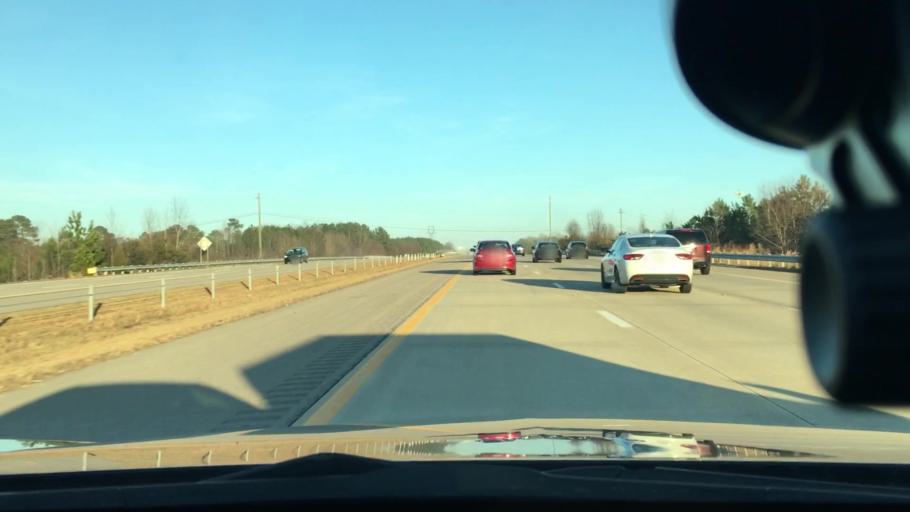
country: US
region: North Carolina
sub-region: Wake County
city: Knightdale
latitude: 35.7670
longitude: -78.4678
